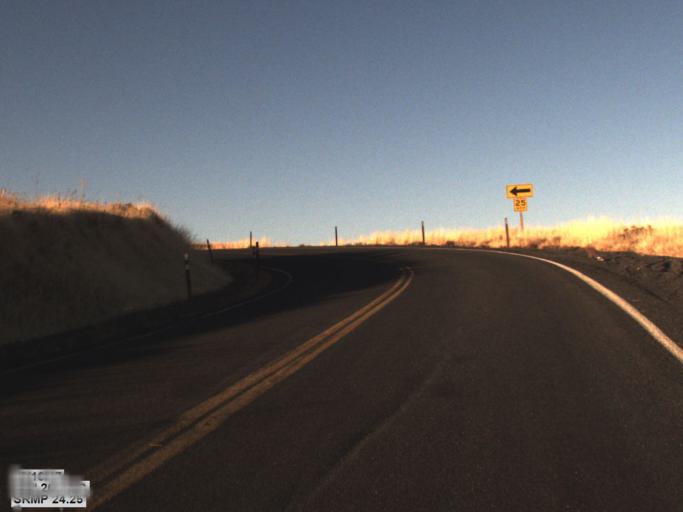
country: US
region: Washington
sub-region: Walla Walla County
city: Waitsburg
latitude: 46.6751
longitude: -118.3300
